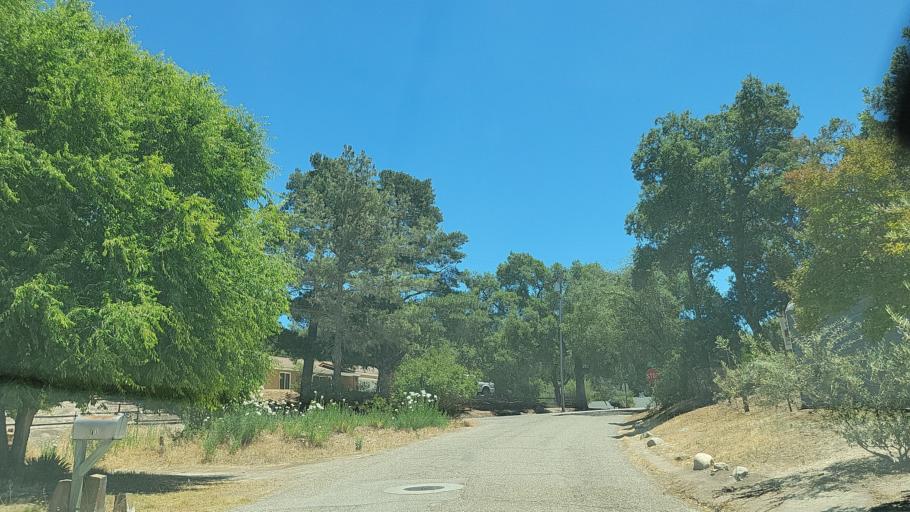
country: US
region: California
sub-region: San Luis Obispo County
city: Atascadero
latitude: 35.4995
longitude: -120.6769
